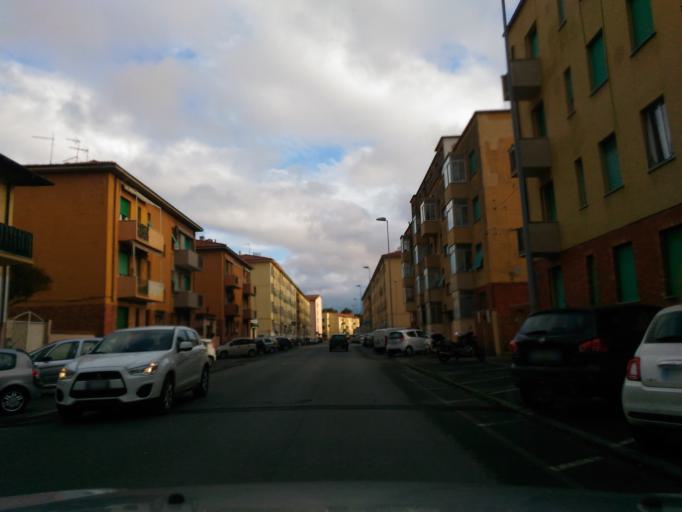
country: IT
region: Tuscany
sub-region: Provincia di Livorno
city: Livorno
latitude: 43.5621
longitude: 10.3312
